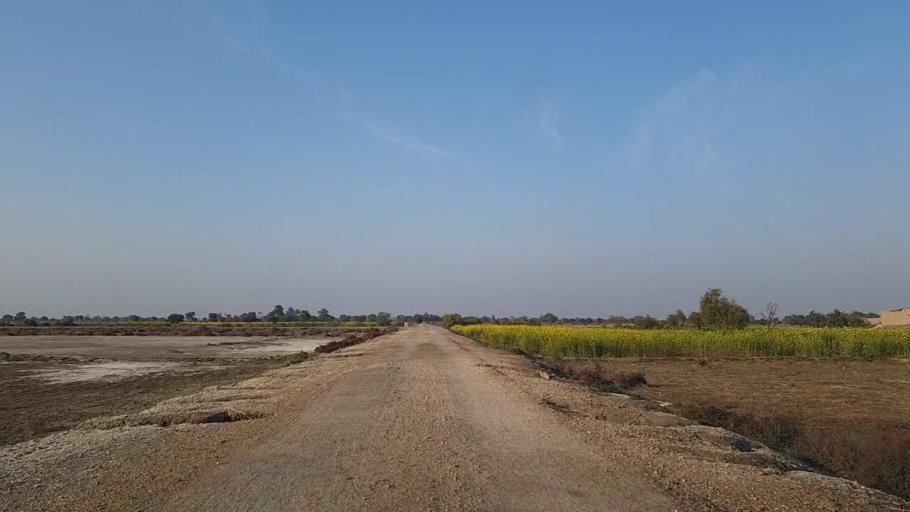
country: PK
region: Sindh
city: Jam Sahib
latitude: 26.3820
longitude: 68.5389
